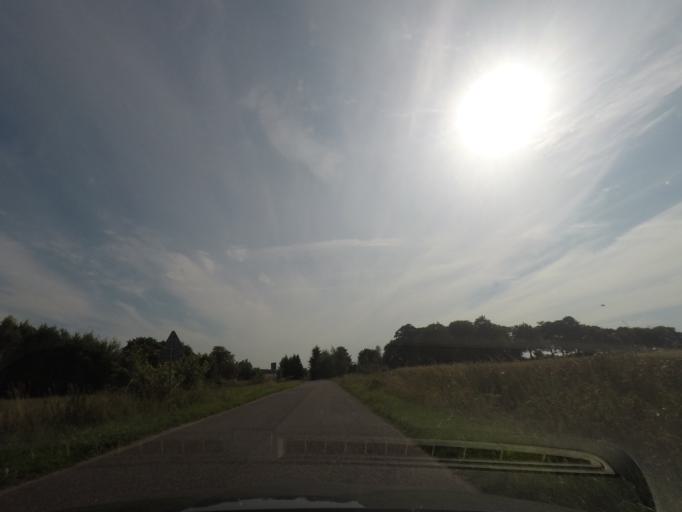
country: PL
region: Pomeranian Voivodeship
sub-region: Powiat slupski
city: Smoldzino
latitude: 54.6279
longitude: 17.2437
